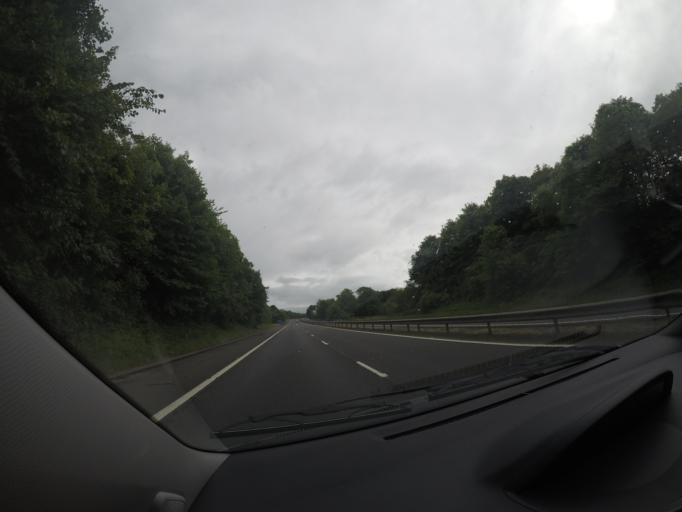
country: GB
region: Scotland
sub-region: Falkirk
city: Dunipace
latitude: 56.0263
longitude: -3.9230
